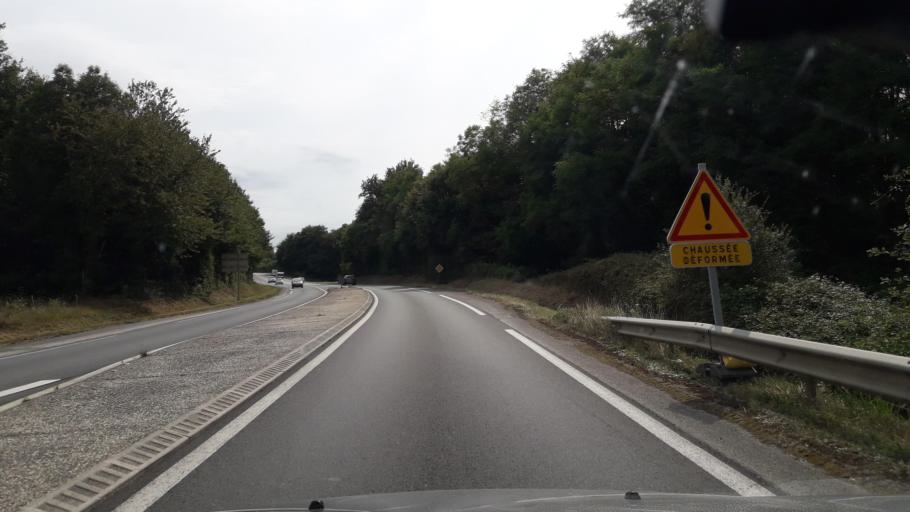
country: FR
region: Poitou-Charentes
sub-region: Departement de la Charente
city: Saint-Claud
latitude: 45.8578
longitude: 0.4651
